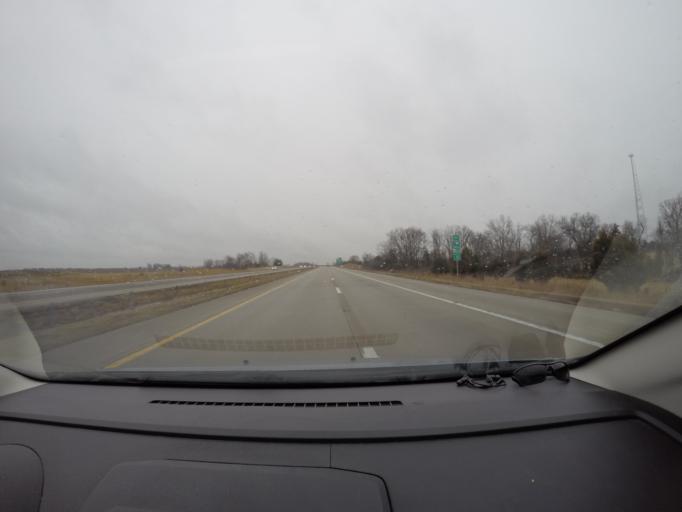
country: US
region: Missouri
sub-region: Callaway County
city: Fulton
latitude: 38.9361
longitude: -91.8146
